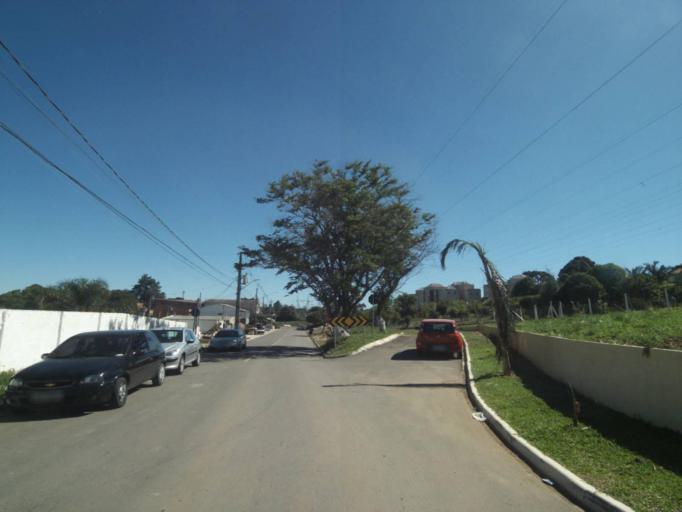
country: BR
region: Parana
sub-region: Curitiba
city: Curitiba
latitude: -25.4881
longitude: -49.3416
